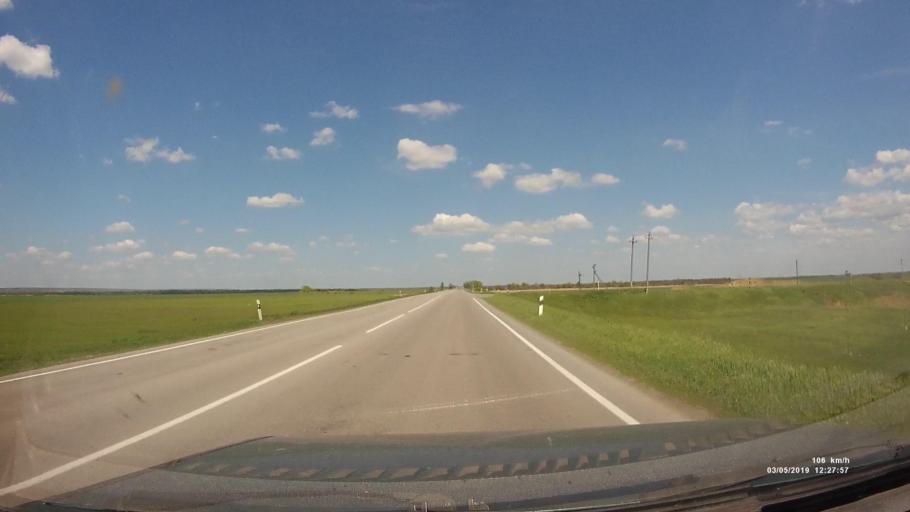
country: RU
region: Rostov
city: Semikarakorsk
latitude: 47.4661
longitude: 40.7245
